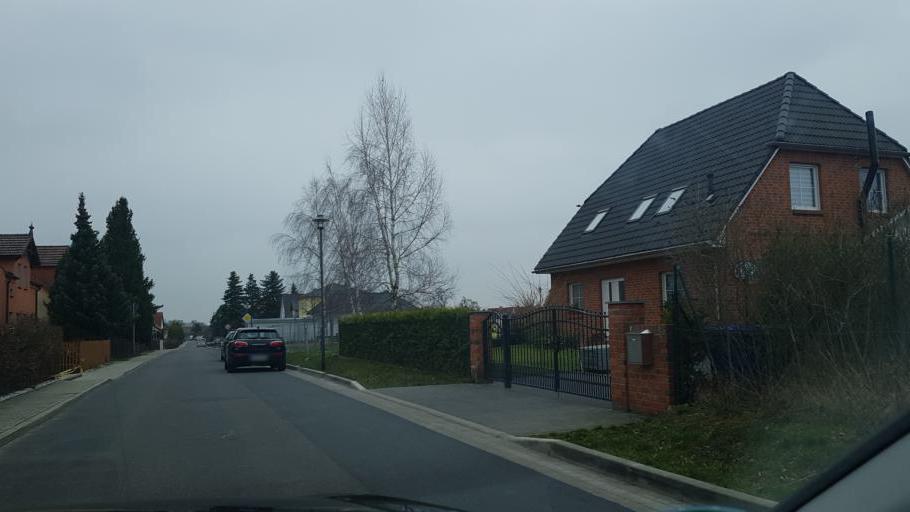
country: DE
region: Brandenburg
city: Mittenwalde
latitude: 52.2904
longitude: 13.5411
